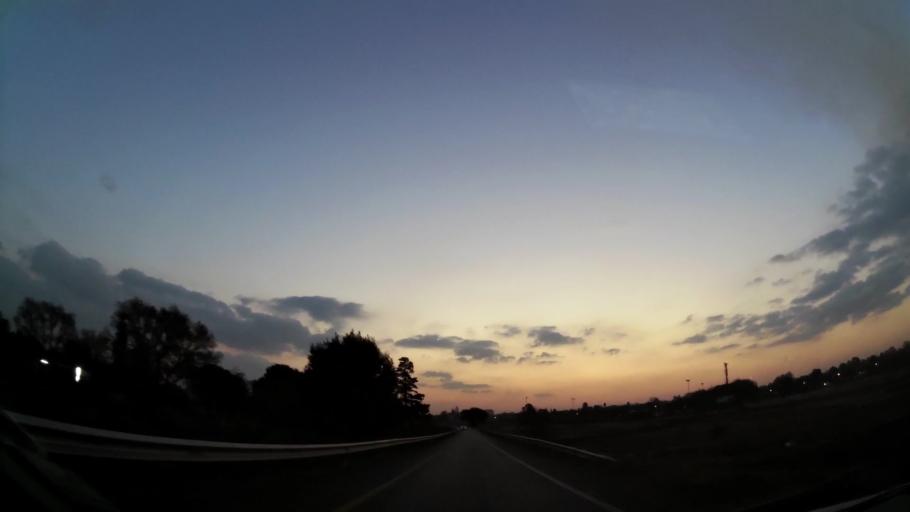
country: ZA
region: Gauteng
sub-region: Ekurhuleni Metropolitan Municipality
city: Springs
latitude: -26.2818
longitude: 28.4512
